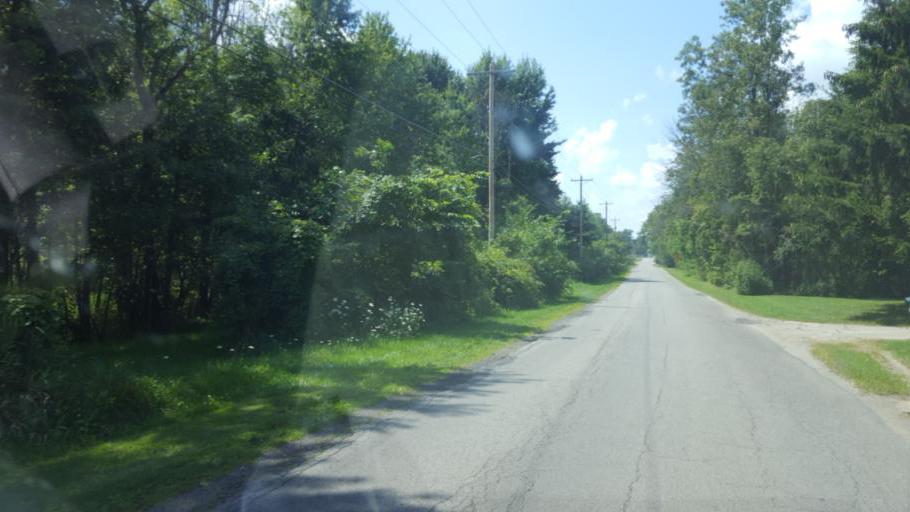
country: US
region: Ohio
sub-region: Knox County
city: Centerburg
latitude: 40.4005
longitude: -82.6920
